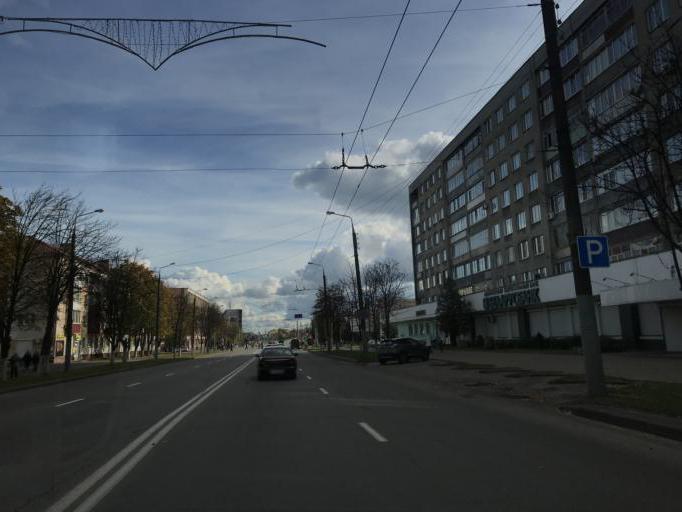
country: BY
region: Gomel
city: Gomel
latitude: 52.4497
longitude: 30.9672
